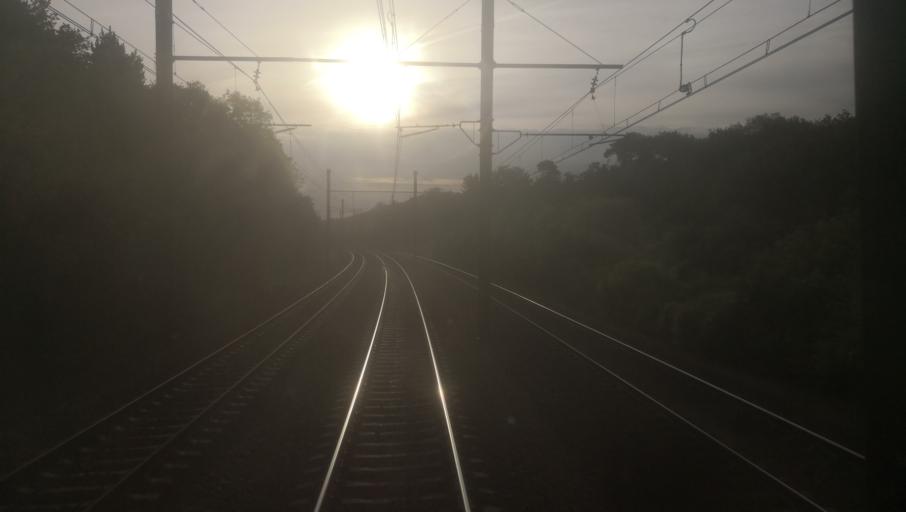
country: FR
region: Ile-de-France
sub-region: Departement de l'Essonne
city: Etampes
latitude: 48.4076
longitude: 2.1100
